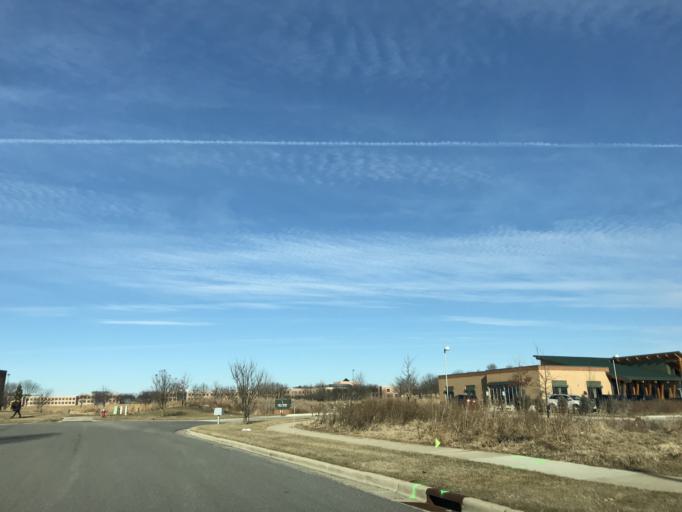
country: US
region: Wisconsin
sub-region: Dane County
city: Sun Prairie
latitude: 43.1520
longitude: -89.2908
